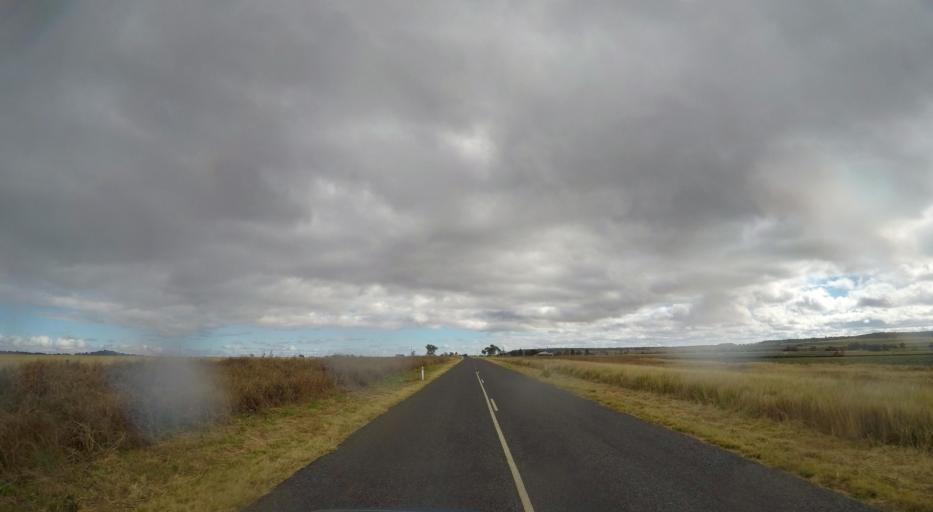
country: AU
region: Queensland
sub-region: Southern Downs
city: Warwick
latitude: -28.0468
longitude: 152.0590
